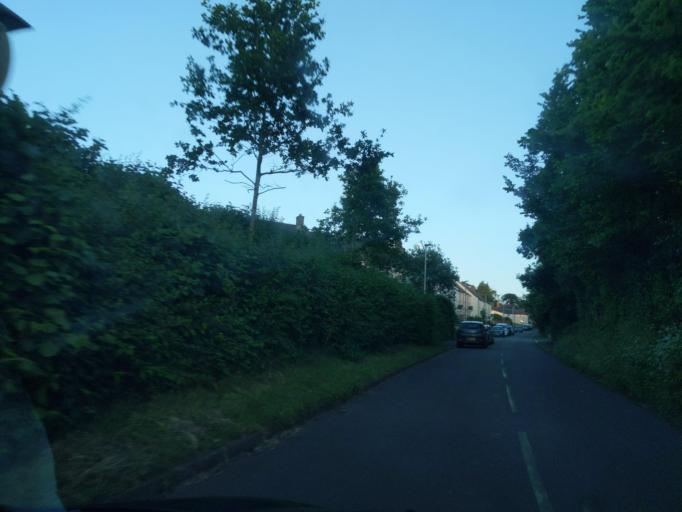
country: GB
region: England
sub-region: Devon
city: Okehampton
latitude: 50.8256
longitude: -4.0727
